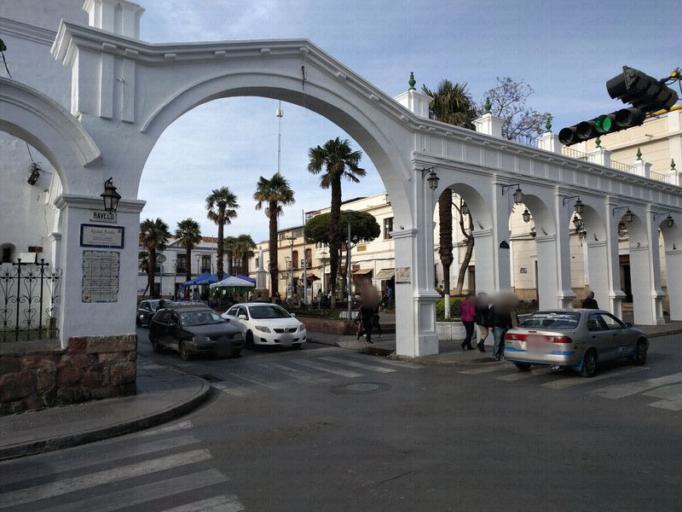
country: BO
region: Chuquisaca
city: Sucre
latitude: -19.0440
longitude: -65.2580
